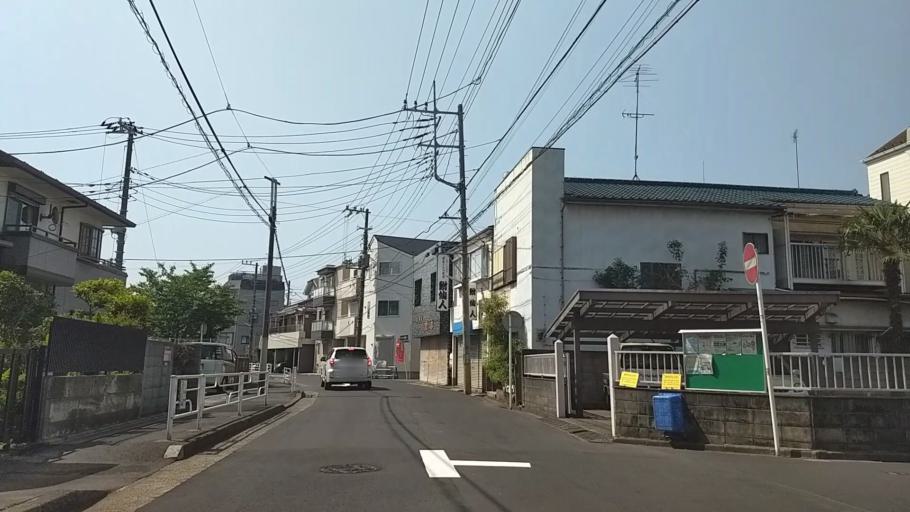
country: JP
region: Kanagawa
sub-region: Kawasaki-shi
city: Kawasaki
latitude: 35.5339
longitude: 139.7343
